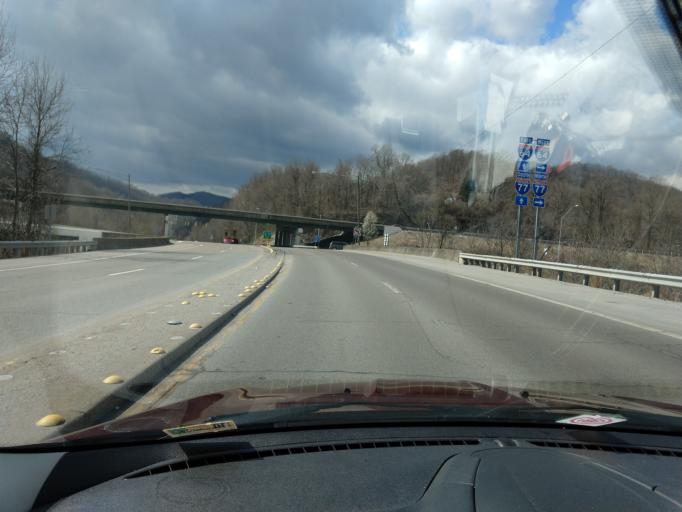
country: US
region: West Virginia
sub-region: Kanawha County
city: Marmet
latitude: 38.2415
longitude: -81.5644
